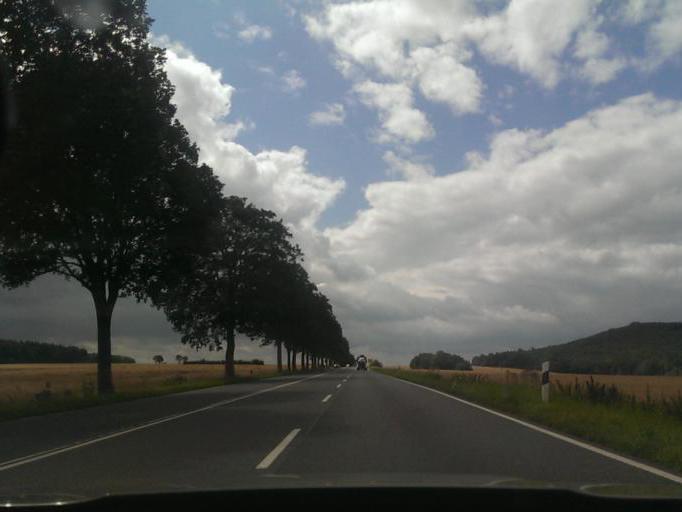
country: DE
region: Lower Saxony
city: Eschershausen
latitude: 51.9174
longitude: 9.6158
